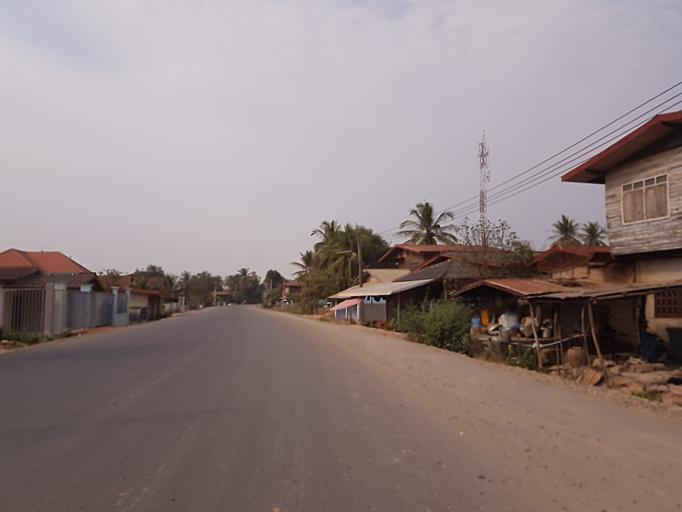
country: TH
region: Nong Khai
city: Nong Khai
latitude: 17.9664
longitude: 102.8391
